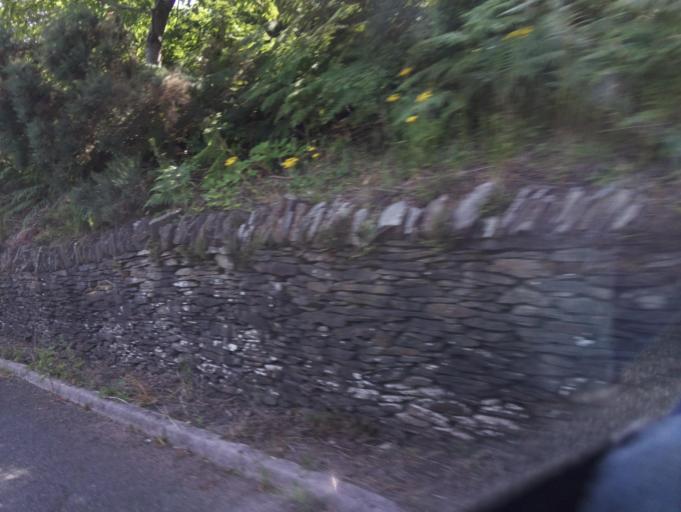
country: GB
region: Wales
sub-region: Caerphilly County Borough
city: New Tredegar
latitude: 51.7222
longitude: -3.2497
